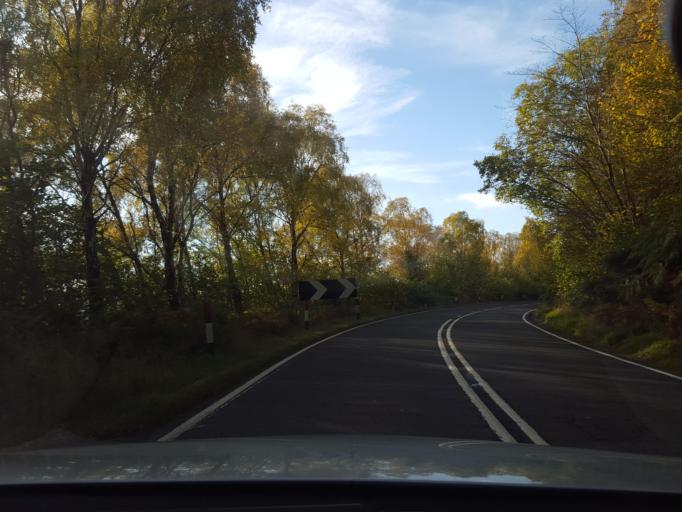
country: GB
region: Scotland
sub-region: Highland
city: Beauly
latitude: 57.3146
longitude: -4.4539
